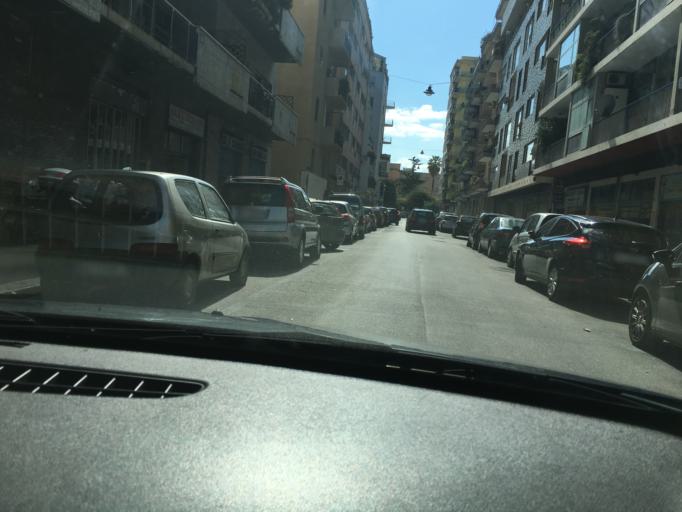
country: IT
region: Apulia
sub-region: Provincia di Bari
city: Bari
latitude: 41.1186
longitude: 16.8873
